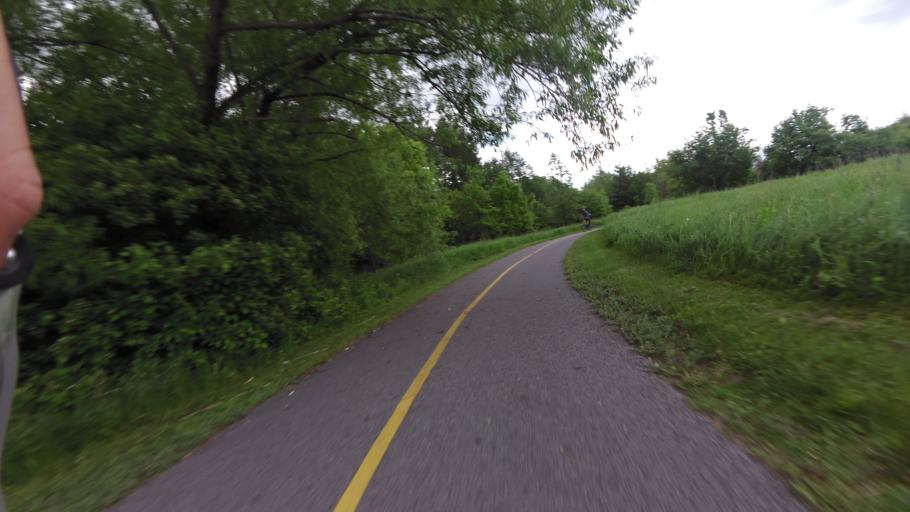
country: CA
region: Ontario
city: Bells Corners
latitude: 45.3326
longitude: -75.8887
